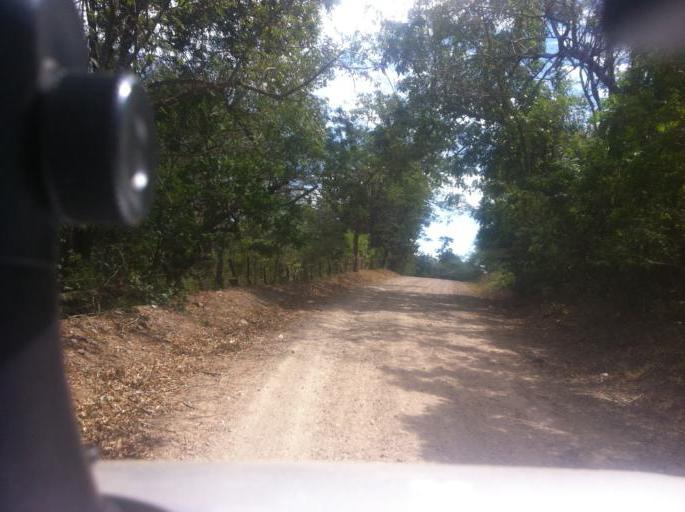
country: NI
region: Granada
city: Nandaime
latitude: 11.6010
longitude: -86.0279
